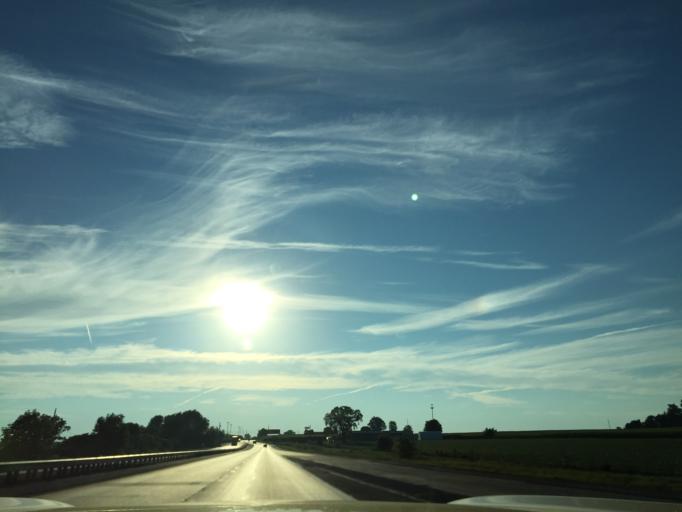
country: US
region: Pennsylvania
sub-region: Berks County
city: Kutztown
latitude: 40.5316
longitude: -75.7569
